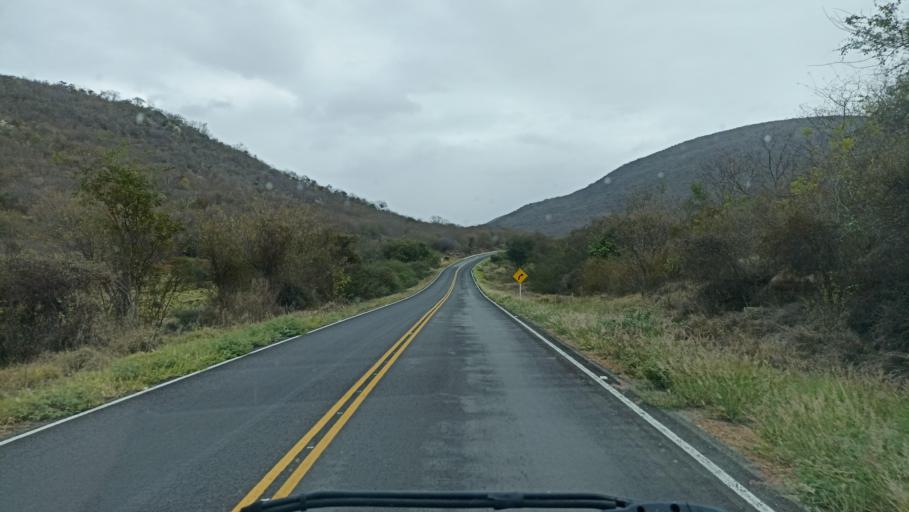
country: BR
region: Bahia
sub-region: Andarai
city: Vera Cruz
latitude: -13.0477
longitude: -40.7786
